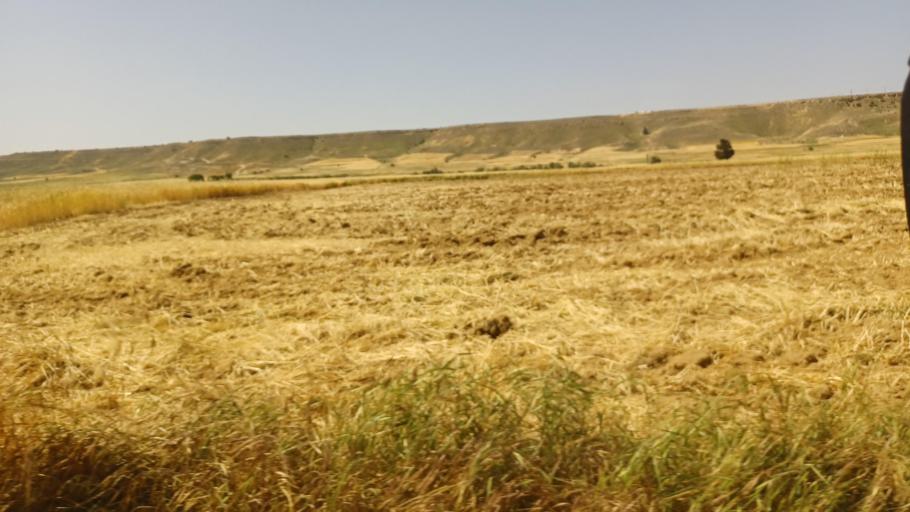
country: CY
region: Lefkosia
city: Mammari
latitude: 35.1808
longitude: 33.2232
